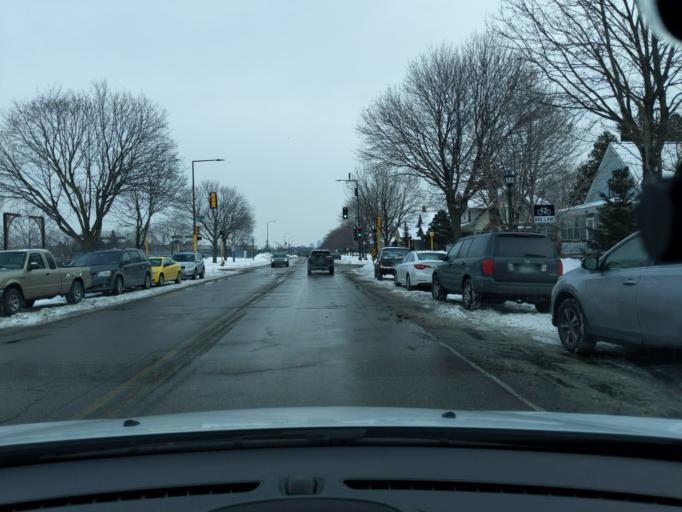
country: US
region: Minnesota
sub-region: Ramsey County
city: Falcon Heights
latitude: 44.9486
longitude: -93.1525
